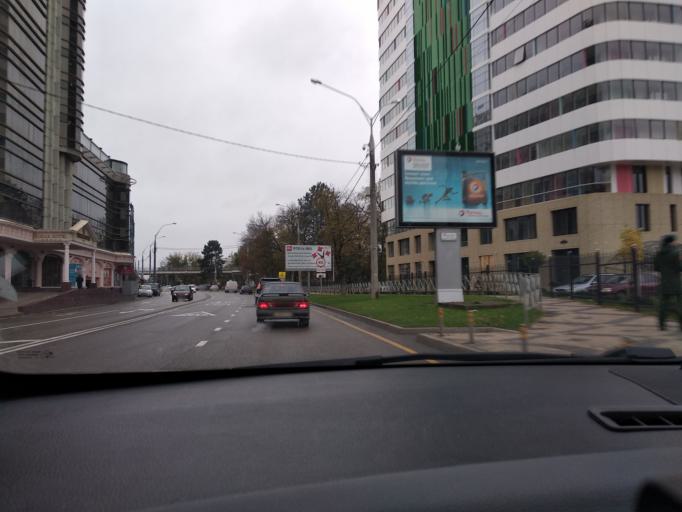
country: RU
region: Krasnodarskiy
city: Krasnodar
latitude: 45.0178
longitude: 38.9591
